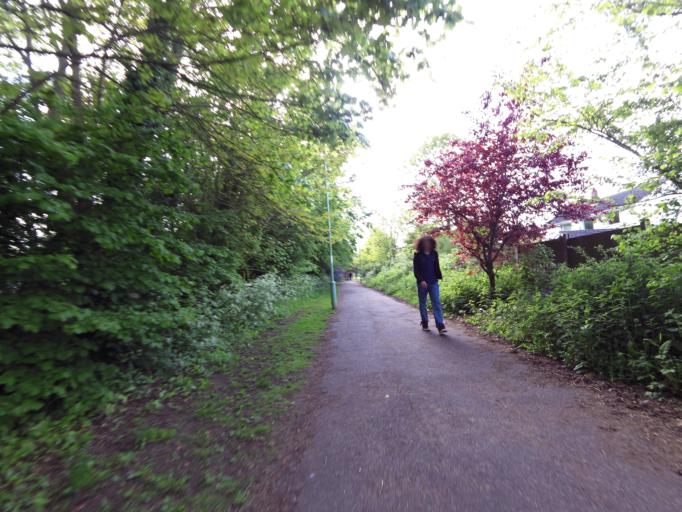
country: GB
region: England
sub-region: Suffolk
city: Beccles
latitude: 52.4496
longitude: 1.5941
